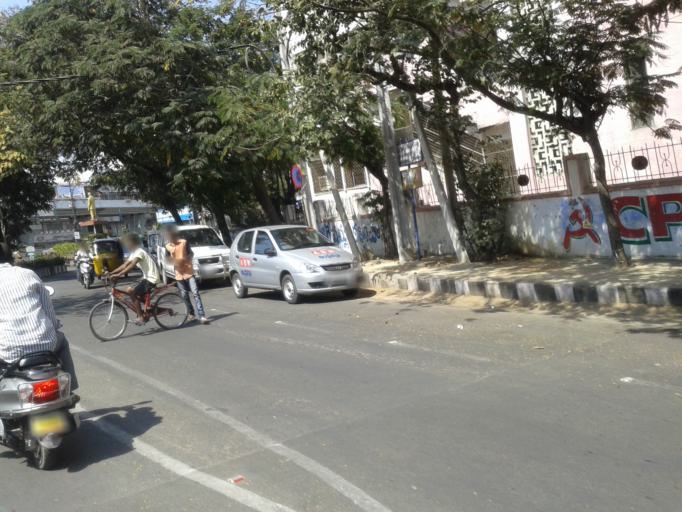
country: IN
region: Telangana
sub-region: Hyderabad
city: Hyderabad
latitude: 17.4005
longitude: 78.4765
